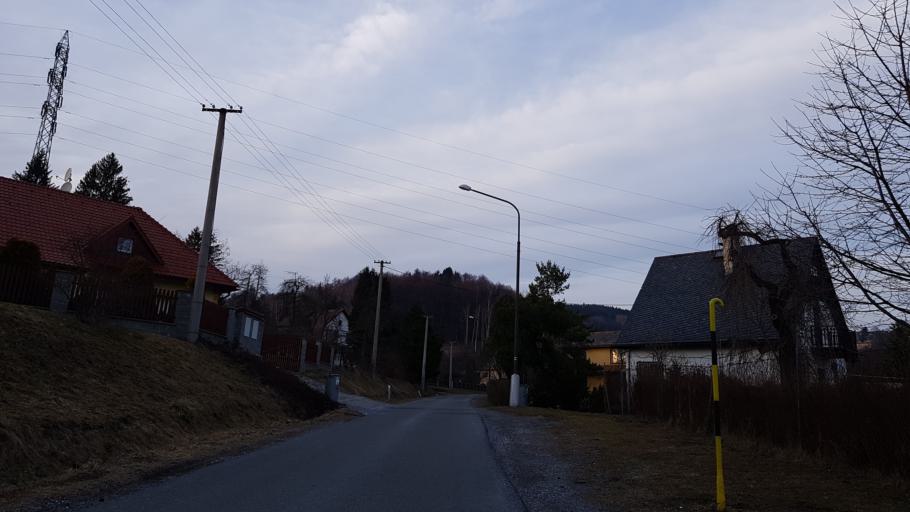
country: CZ
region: Olomoucky
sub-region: Okres Jesenik
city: Jesenik
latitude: 50.2301
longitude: 17.1855
